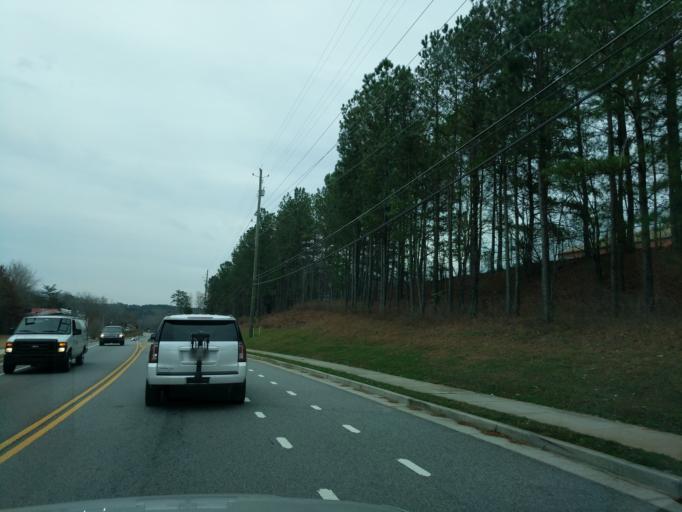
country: US
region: Georgia
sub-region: Fulton County
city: Alpharetta
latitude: 34.0528
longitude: -84.2742
